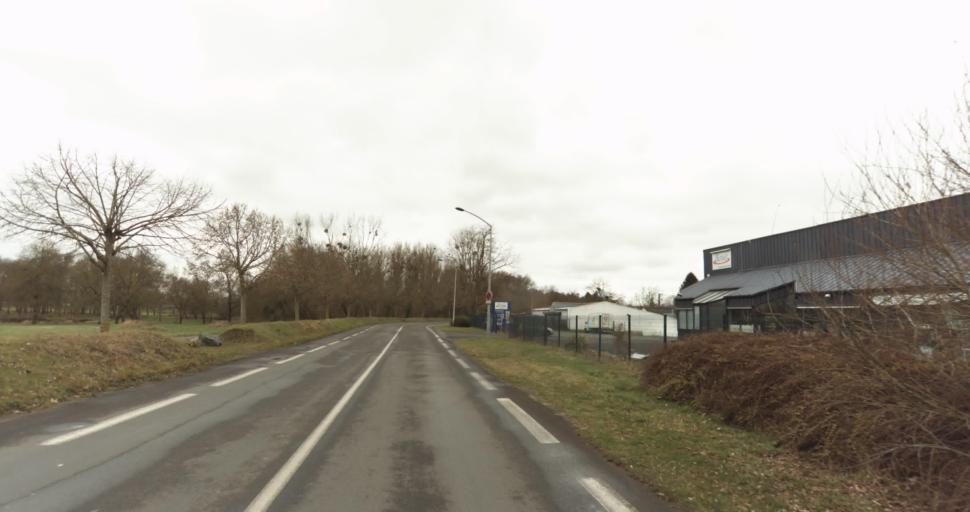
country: FR
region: Pays de la Loire
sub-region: Departement de Maine-et-Loire
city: Saumur
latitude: 47.2497
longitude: -0.0862
